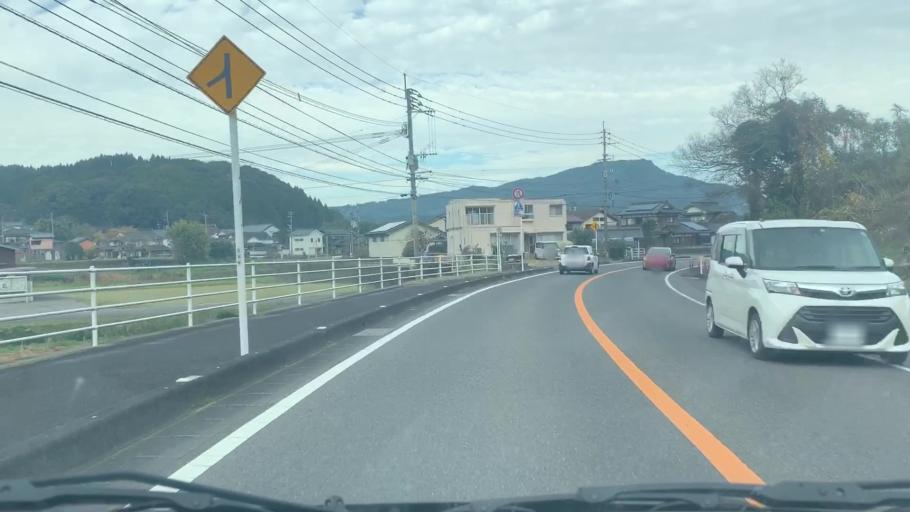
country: JP
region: Saga Prefecture
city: Imaricho-ko
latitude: 33.2668
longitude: 129.9644
